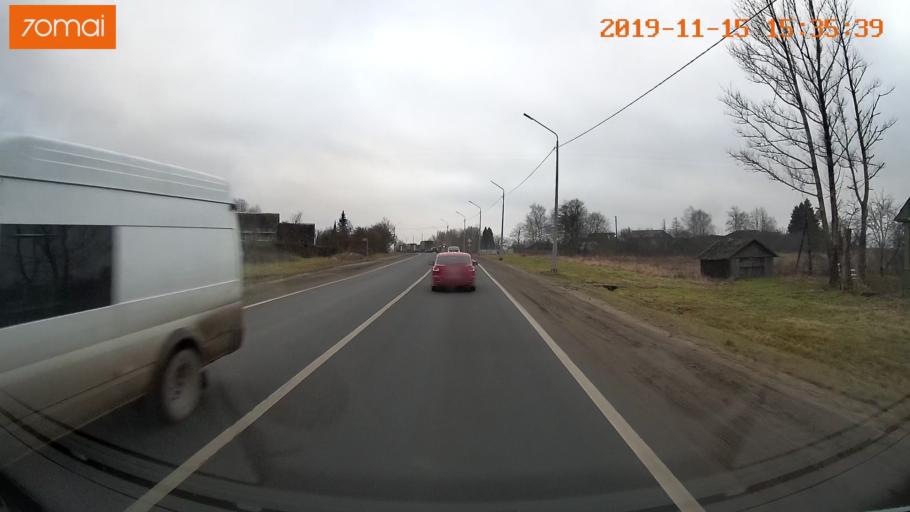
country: RU
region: Jaroslavl
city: Danilov
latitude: 58.0568
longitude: 40.0876
